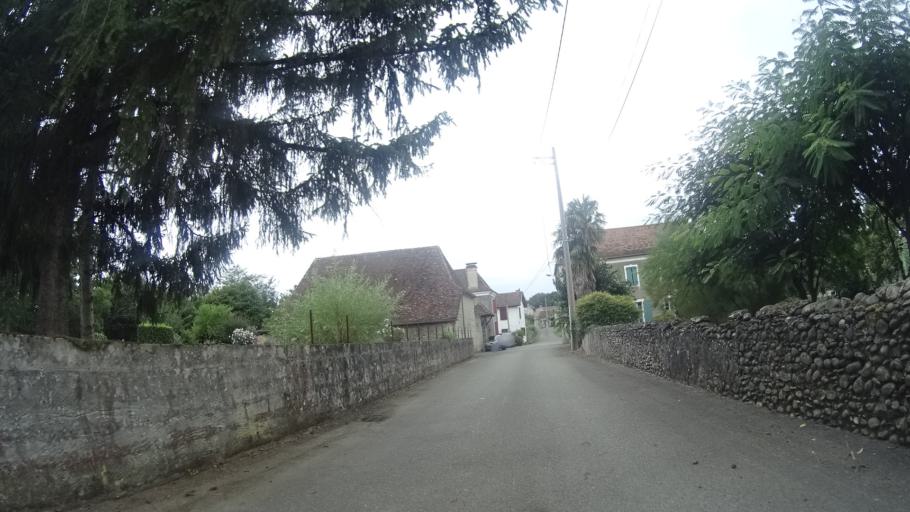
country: FR
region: Aquitaine
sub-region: Departement des Pyrenees-Atlantiques
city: Orthez
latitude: 43.4694
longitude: -0.7191
